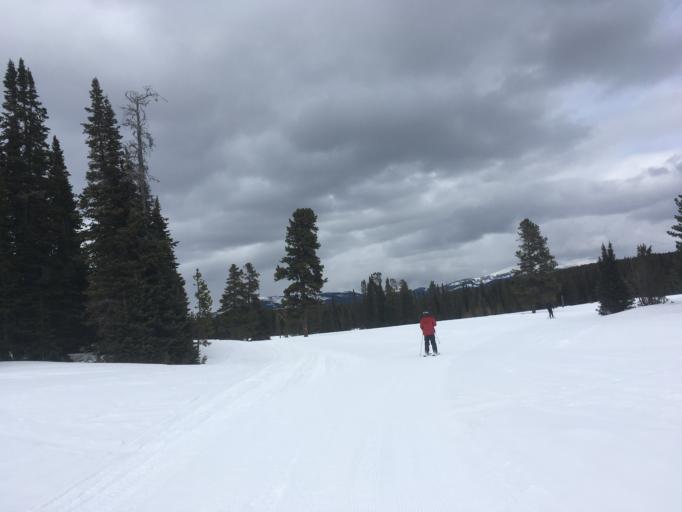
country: US
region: Montana
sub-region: Meagher County
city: White Sulphur Springs
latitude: 46.8513
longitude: -110.7020
